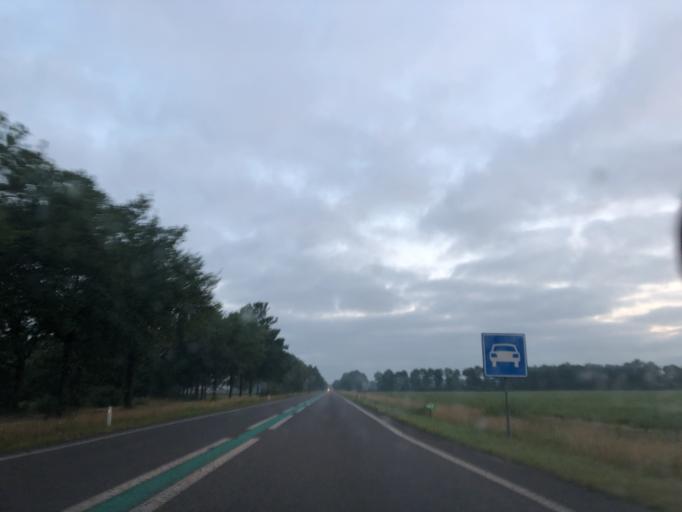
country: NL
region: Drenthe
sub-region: Gemeente Borger-Odoorn
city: Borger
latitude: 52.9794
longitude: 6.7733
